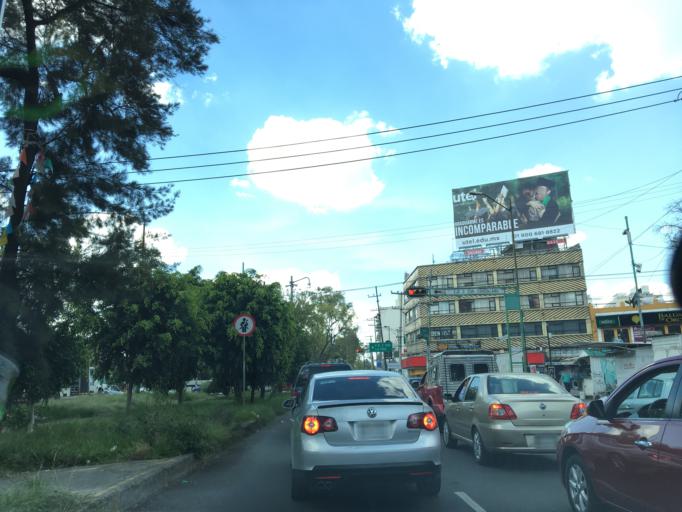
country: MX
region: Mexico City
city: Mexico City
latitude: 19.4084
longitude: -99.1265
